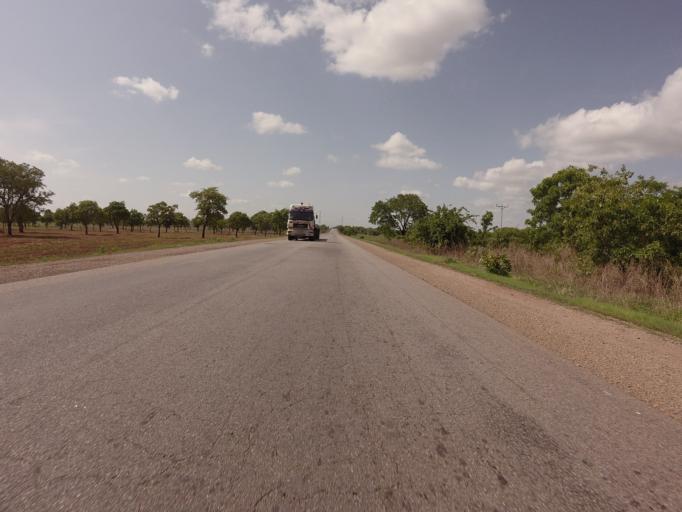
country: GH
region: Northern
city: Savelugu
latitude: 9.9701
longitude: -0.8290
